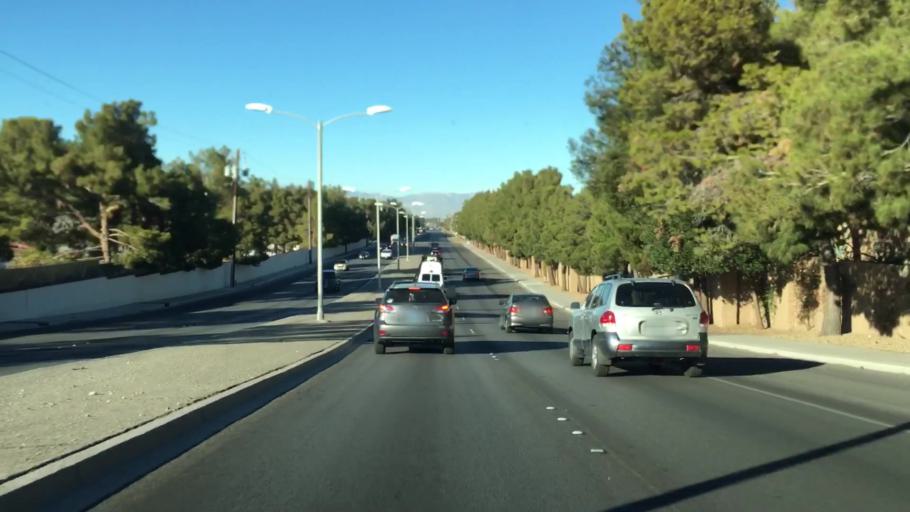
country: US
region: Nevada
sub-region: Clark County
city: Whitney
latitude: 36.0583
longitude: -115.1003
